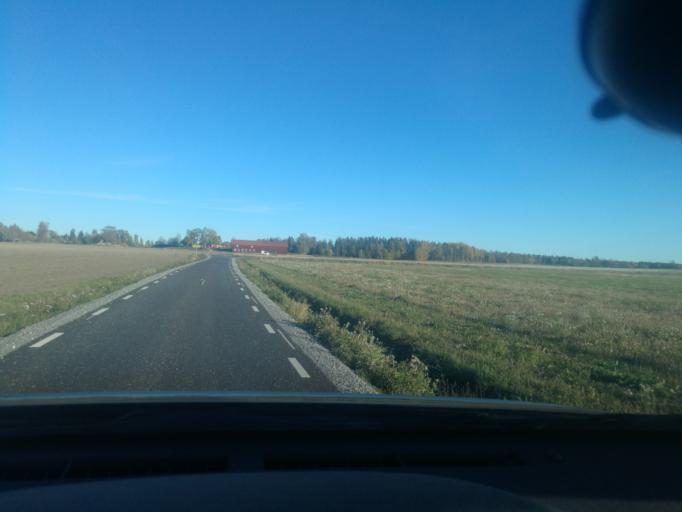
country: SE
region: Vaestmanland
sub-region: Kopings Kommun
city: Koping
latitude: 59.5661
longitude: 16.0551
